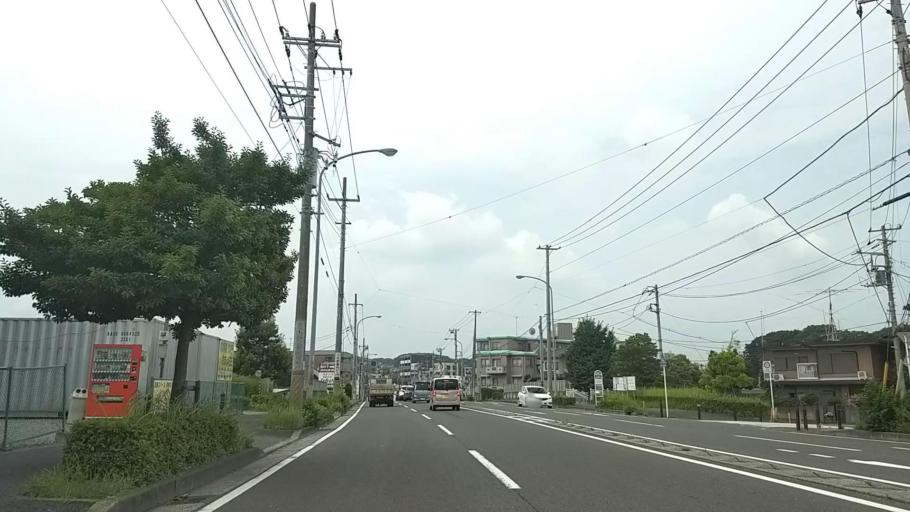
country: JP
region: Tokyo
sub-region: Machida-shi
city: Machida
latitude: 35.5123
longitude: 139.5476
